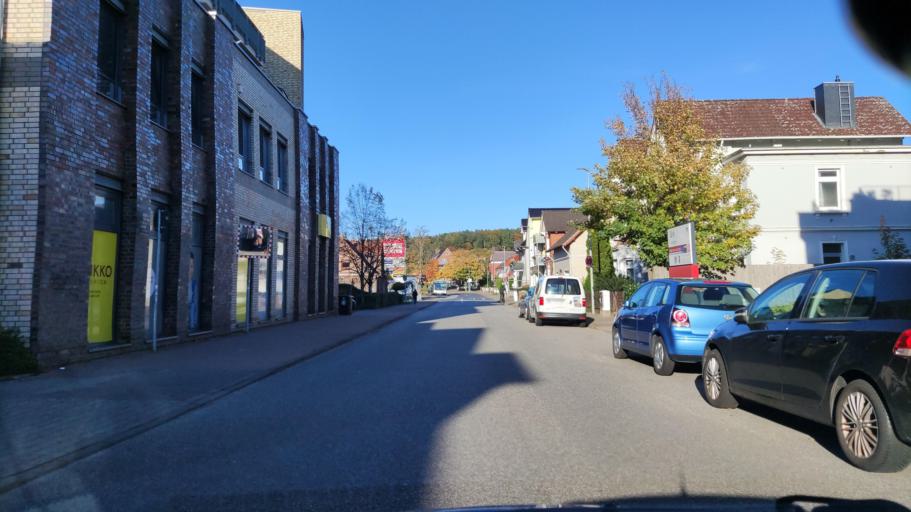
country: DE
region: Schleswig-Holstein
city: Geesthacht
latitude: 53.4346
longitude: 10.3726
